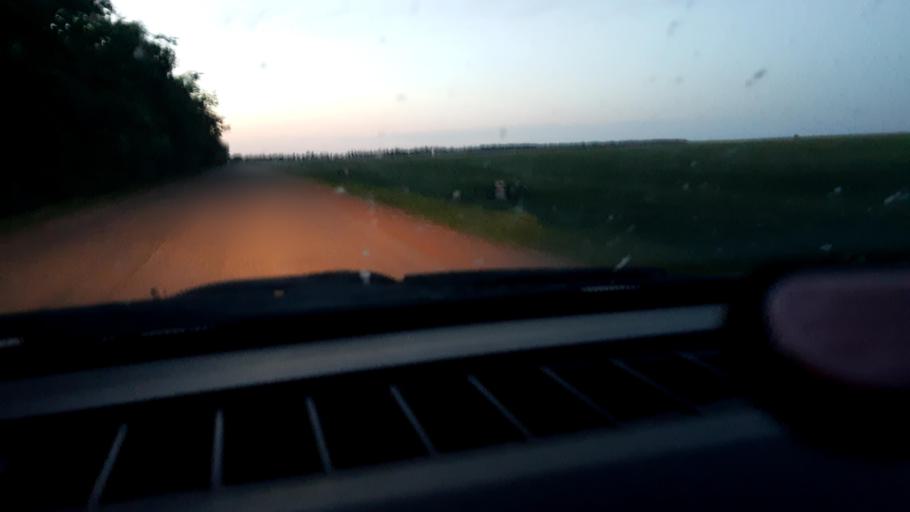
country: RU
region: Bashkortostan
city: Asanovo
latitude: 54.8181
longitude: 55.5937
